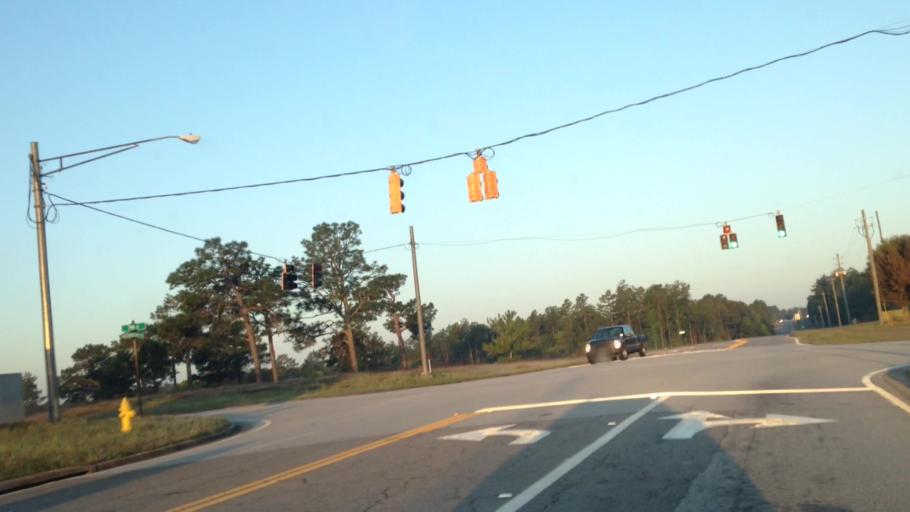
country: US
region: Georgia
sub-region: Columbia County
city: Grovetown
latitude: 33.4257
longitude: -82.1628
